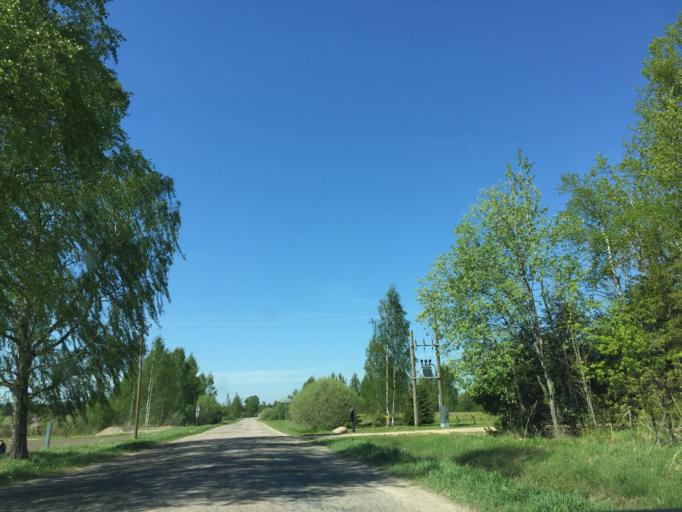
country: LV
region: Kegums
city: Kegums
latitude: 56.8520
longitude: 24.7155
